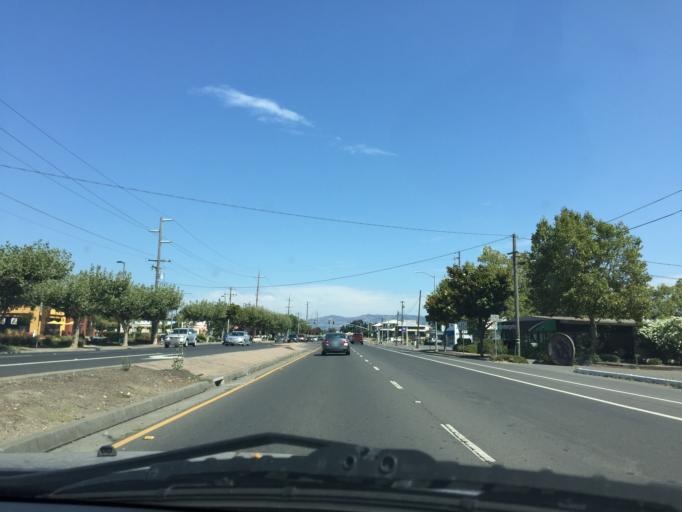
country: US
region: California
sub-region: Napa County
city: Napa
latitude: 38.2829
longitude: -122.2744
